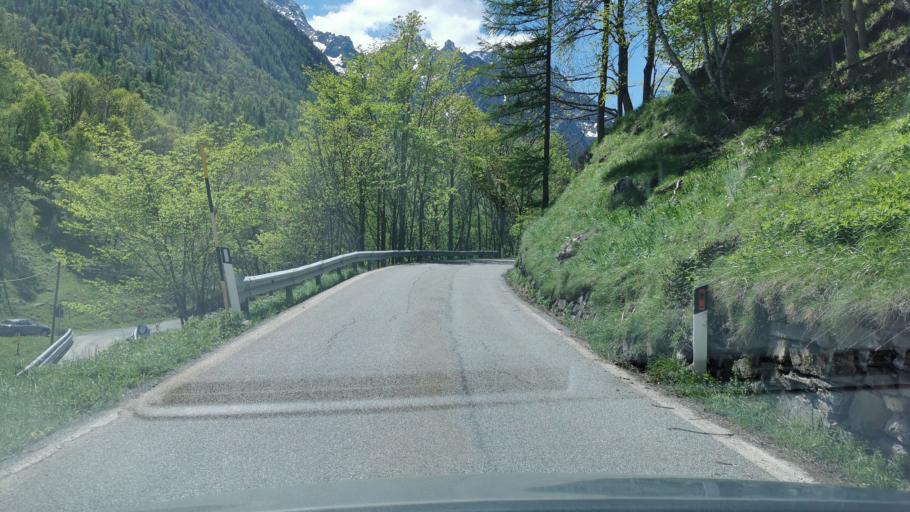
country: IT
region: Piedmont
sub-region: Provincia di Torino
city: Usseglio
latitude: 45.2255
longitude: 7.1981
